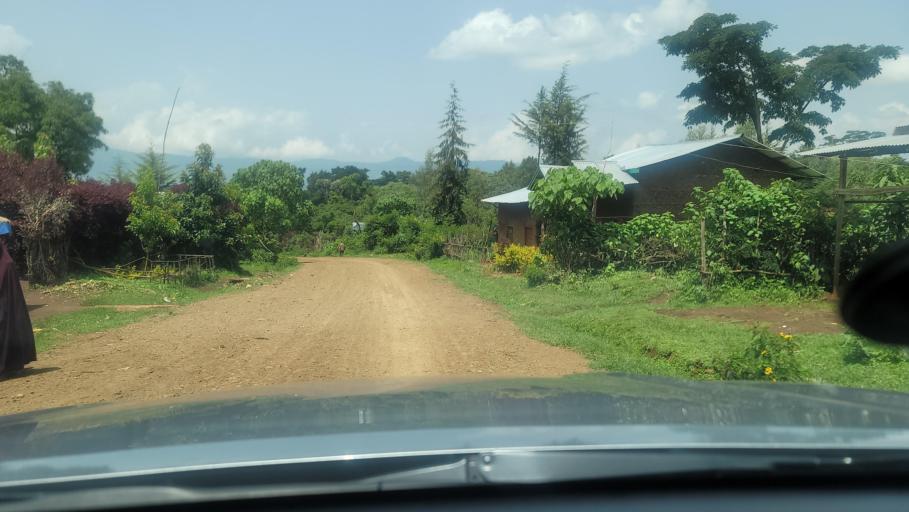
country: ET
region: Oromiya
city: Agaro
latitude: 7.7968
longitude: 36.4169
